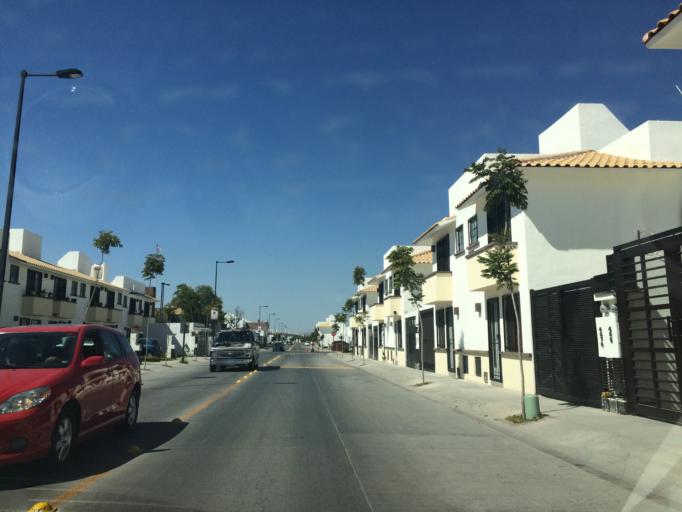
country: MX
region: Guanajuato
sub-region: Leon
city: San Jose de Duran (Los Troncoso)
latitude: 21.0880
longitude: -101.6516
